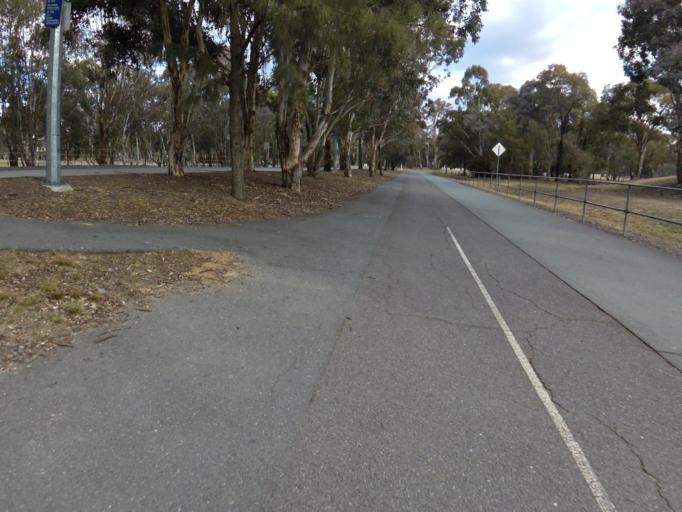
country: AU
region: Australian Capital Territory
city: Kaleen
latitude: -35.2493
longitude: 149.1050
